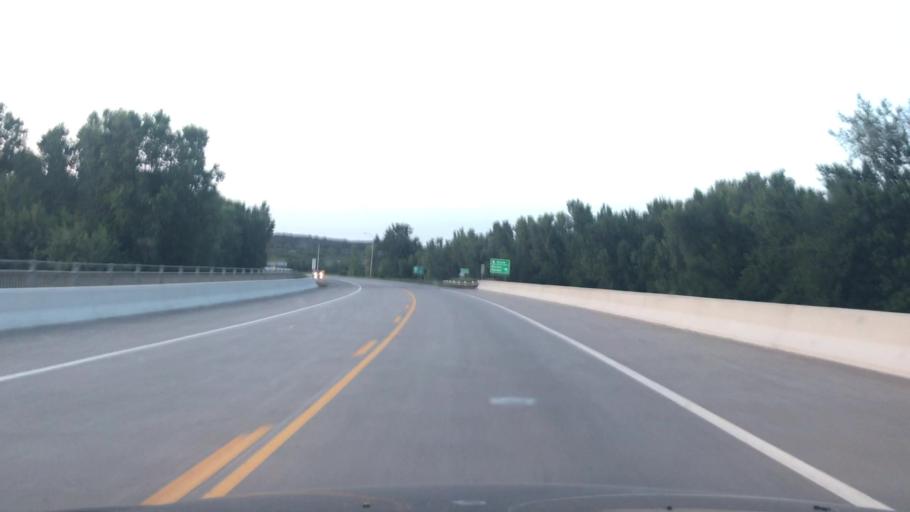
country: US
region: Minnesota
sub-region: Redwood County
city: Redwood Falls
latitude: 44.5455
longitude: -94.9951
